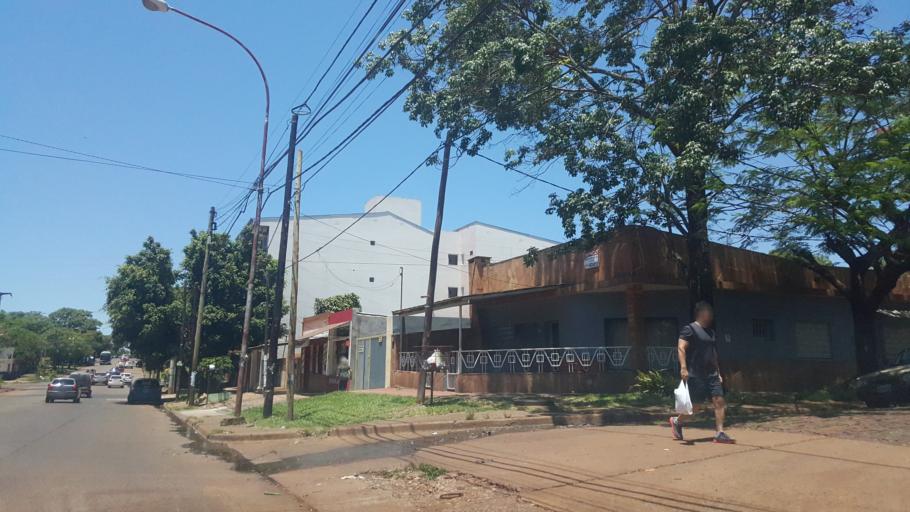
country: AR
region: Misiones
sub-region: Departamento de Capital
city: Posadas
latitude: -27.3726
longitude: -55.9145
